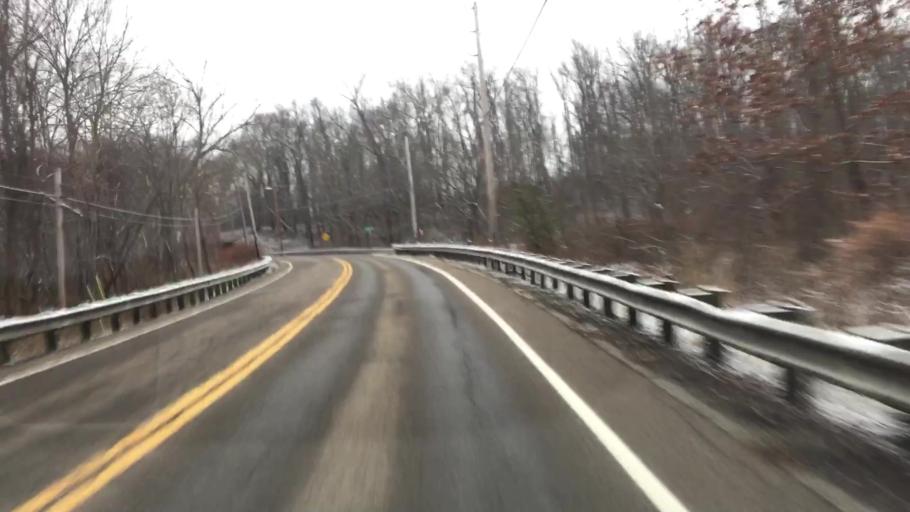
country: US
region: Ohio
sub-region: Summit County
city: Norton
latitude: 41.0709
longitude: -81.6396
